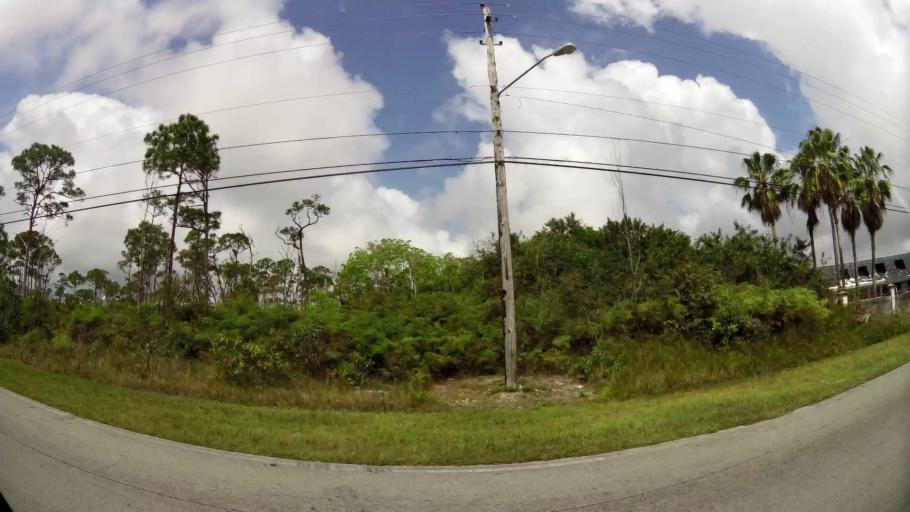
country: BS
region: Freeport
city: Lucaya
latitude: 26.5287
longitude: -78.6207
